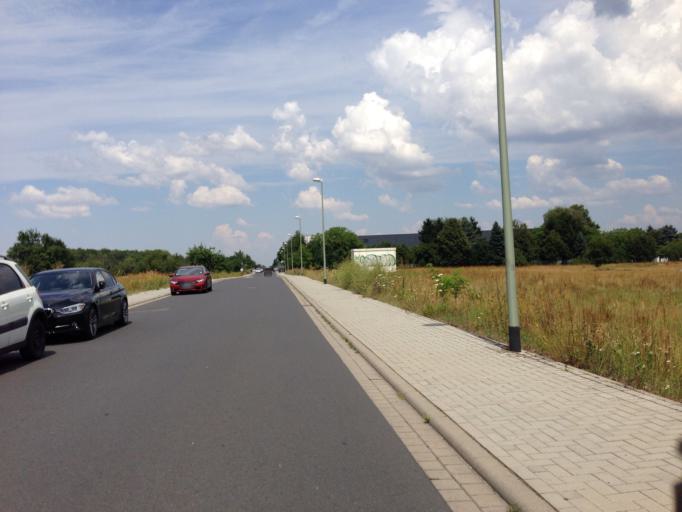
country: DE
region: Hesse
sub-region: Regierungsbezirk Darmstadt
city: Hanau am Main
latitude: 50.1054
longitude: 8.8958
